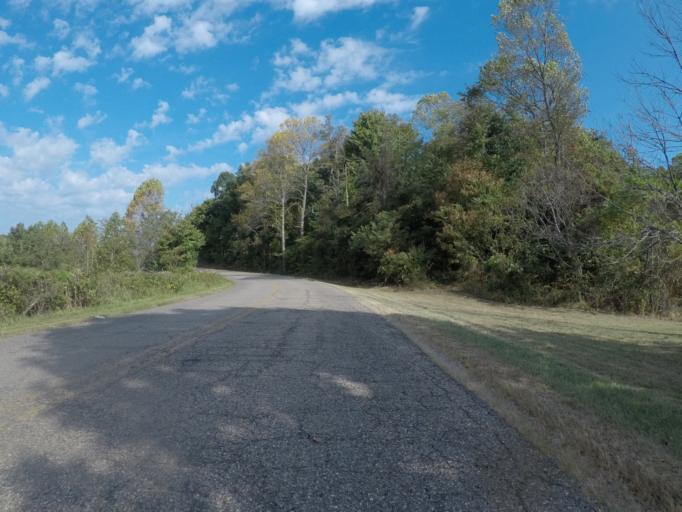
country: US
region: West Virginia
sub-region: Cabell County
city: Lesage
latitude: 38.5925
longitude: -82.4224
